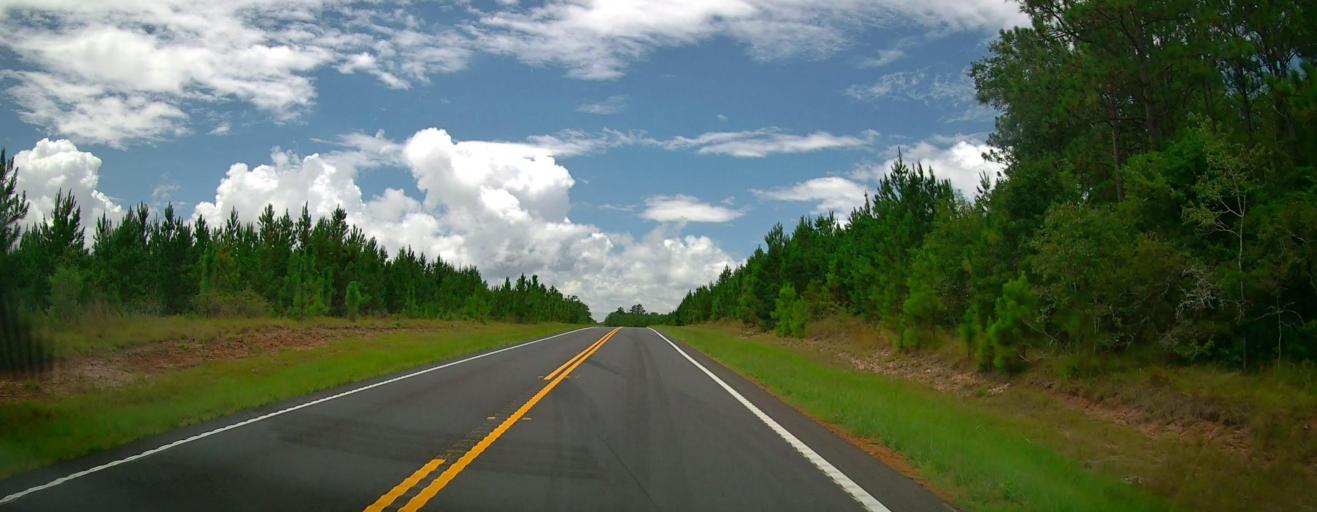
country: US
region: Georgia
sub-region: Dooly County
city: Vienna
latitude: 32.0770
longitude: -83.6192
